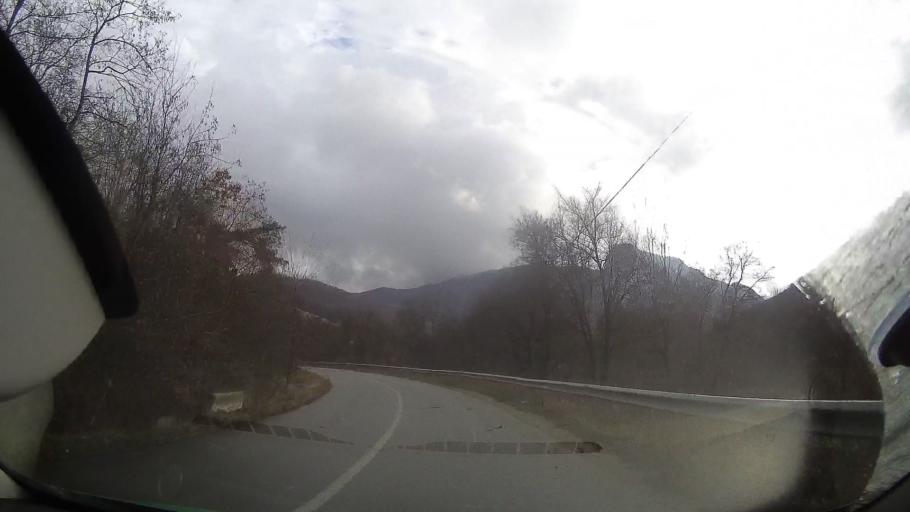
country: RO
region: Alba
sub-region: Comuna Rimetea
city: Rimetea
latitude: 46.4792
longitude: 23.5810
